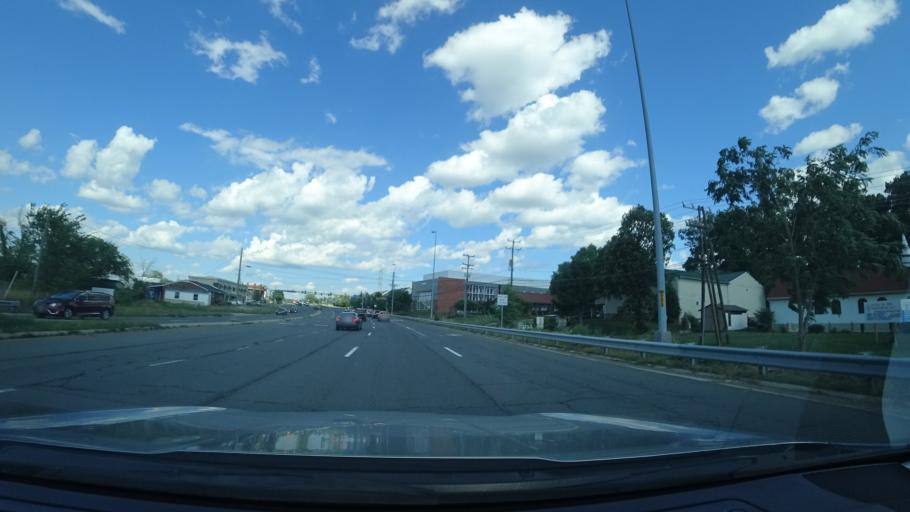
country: US
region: Virginia
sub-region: Loudoun County
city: Sterling
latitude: 39.0047
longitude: -77.4310
